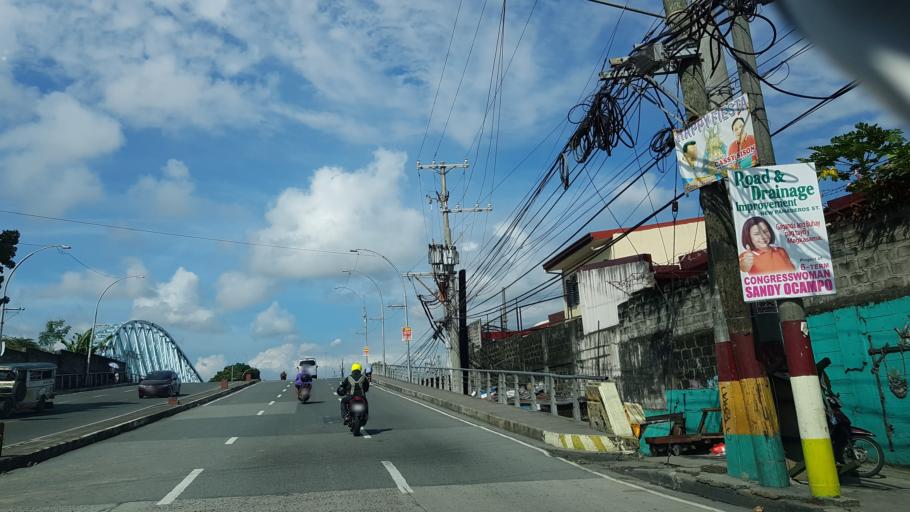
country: PH
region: Metro Manila
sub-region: San Juan
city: San Juan
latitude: 14.5856
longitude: 121.0191
